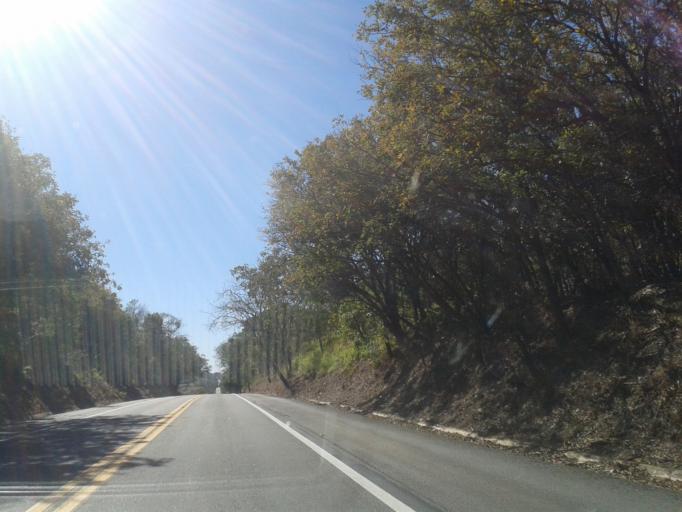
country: BR
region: Goias
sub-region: Goias
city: Goias
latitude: -15.7165
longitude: -50.1891
